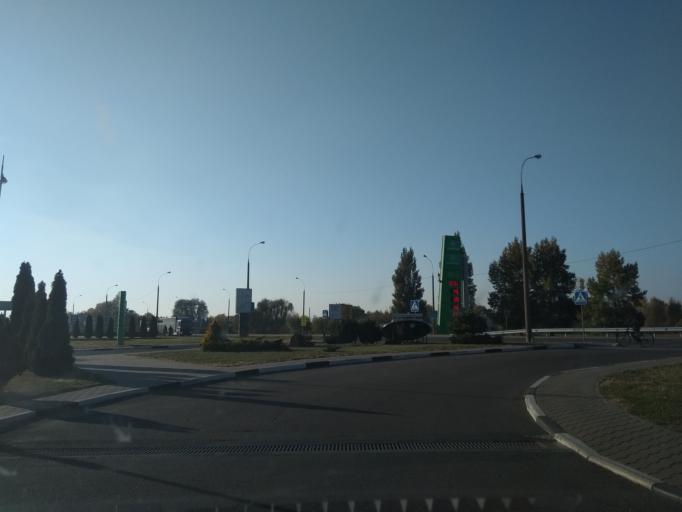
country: BY
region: Brest
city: Brest
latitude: 52.0773
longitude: 23.7233
